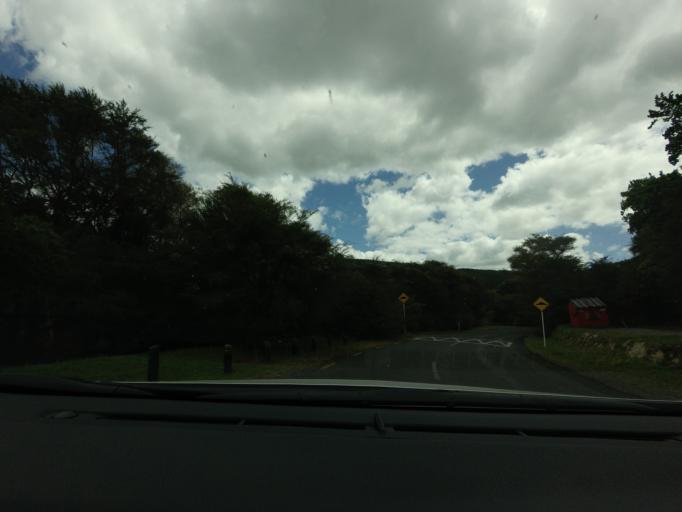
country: NZ
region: Bay of Plenty
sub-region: Rotorua District
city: Rotorua
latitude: -38.3559
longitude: 176.3668
